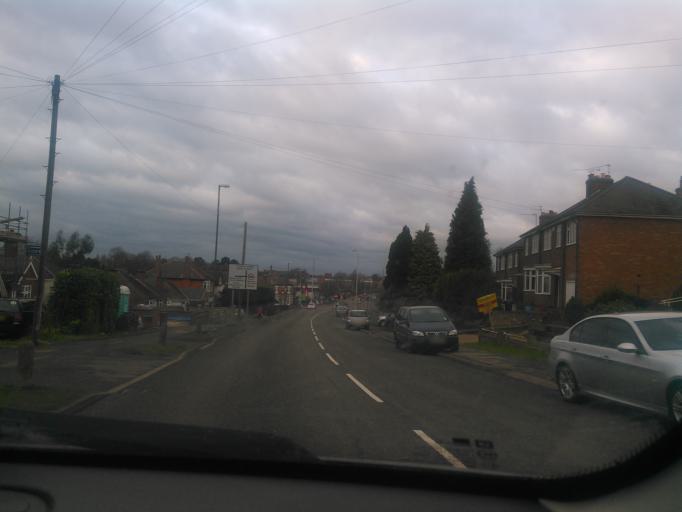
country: GB
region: England
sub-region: Leicestershire
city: Wigston Magna
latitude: 52.5799
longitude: -1.1022
